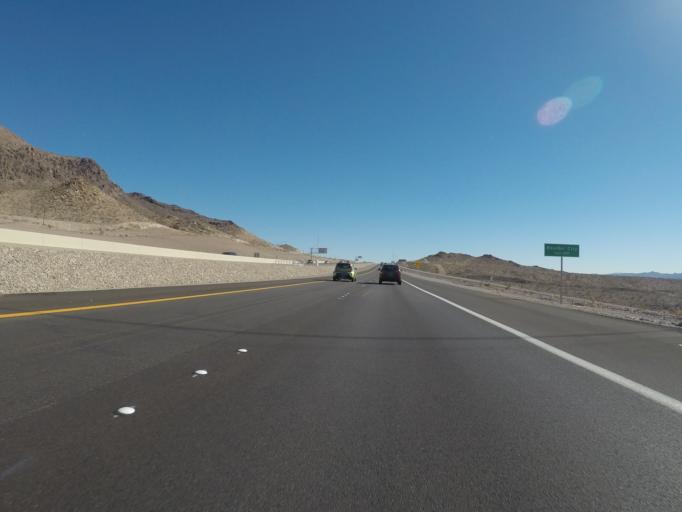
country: US
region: Nevada
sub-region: Clark County
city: Boulder City
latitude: 35.9681
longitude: -114.9087
